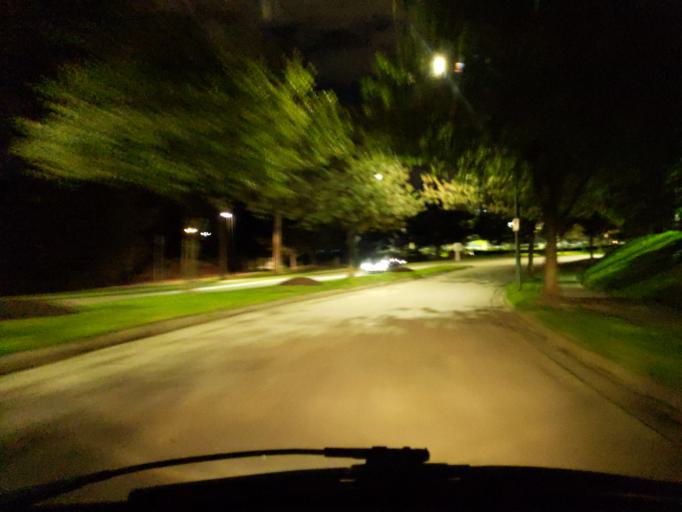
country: CA
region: British Columbia
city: Burnaby
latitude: 49.2608
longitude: -123.0130
